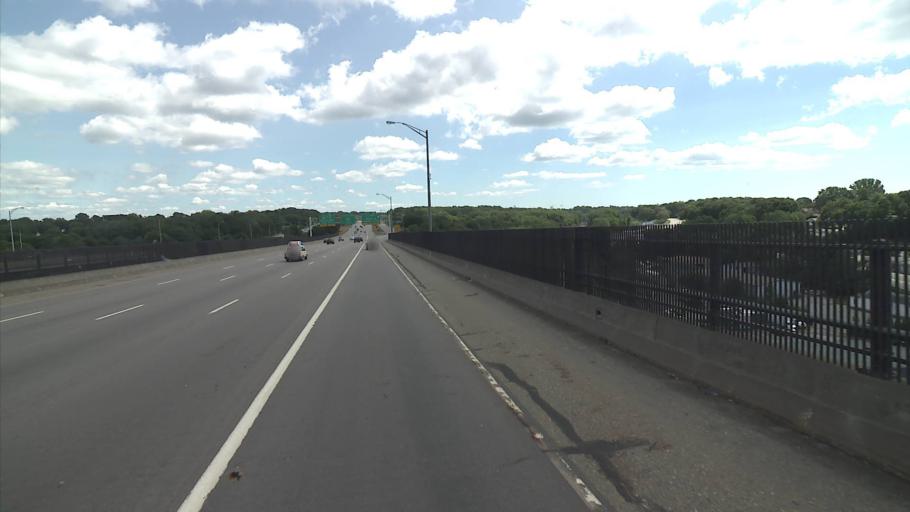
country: US
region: Connecticut
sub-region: New London County
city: Groton
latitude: 41.3640
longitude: -72.0829
